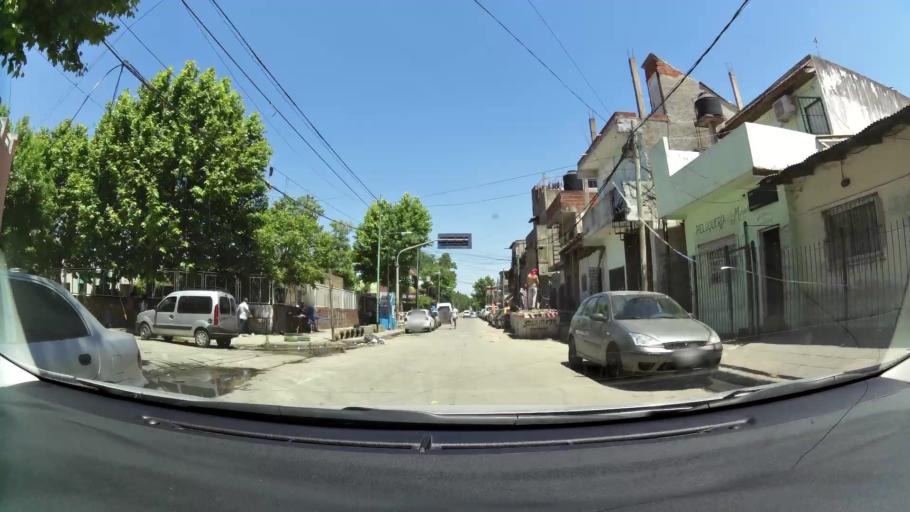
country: AR
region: Buenos Aires
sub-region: Partido de Avellaneda
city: Avellaneda
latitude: -34.6532
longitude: -58.3953
